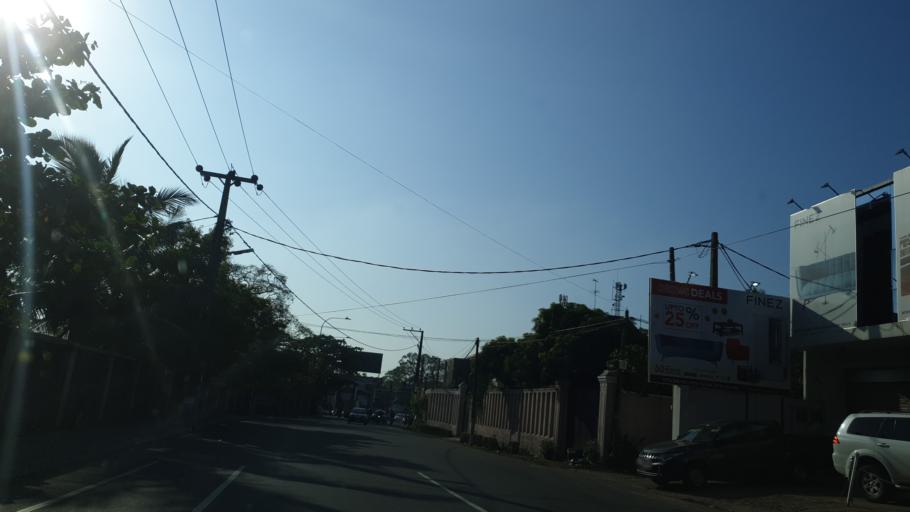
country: LK
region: Western
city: Sri Jayewardenepura Kotte
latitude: 6.8564
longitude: 79.8921
